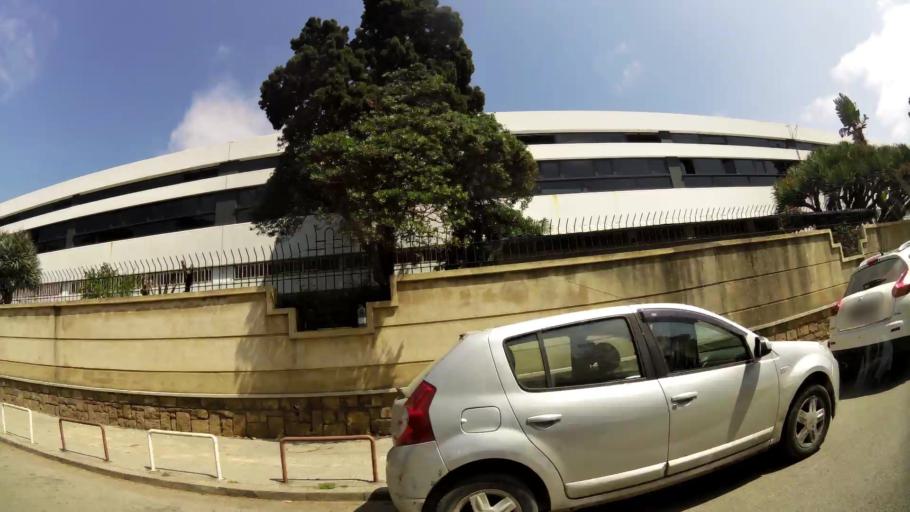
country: MA
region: Rabat-Sale-Zemmour-Zaer
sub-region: Rabat
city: Rabat
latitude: 33.9932
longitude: -6.8451
